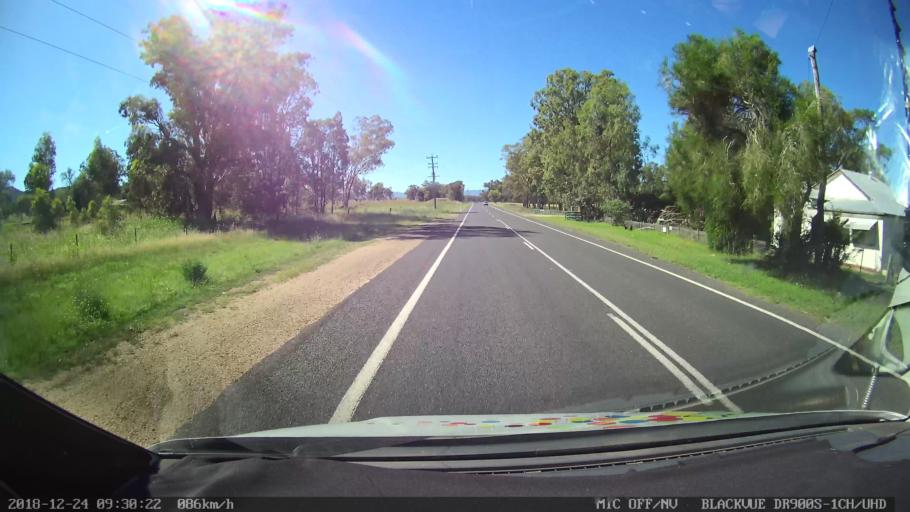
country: AU
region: New South Wales
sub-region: Liverpool Plains
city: Quirindi
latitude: -31.5614
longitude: 150.6972
